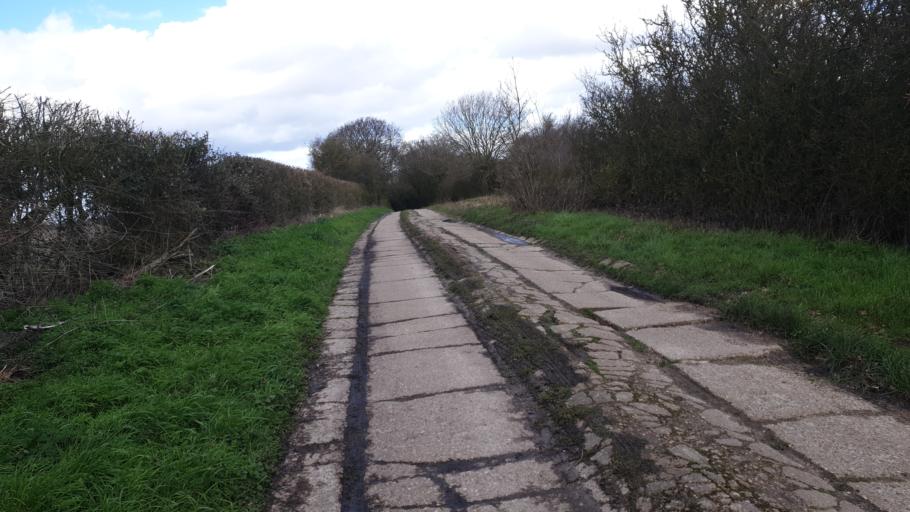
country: GB
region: England
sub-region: Essex
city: Little Clacton
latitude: 51.8306
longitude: 1.1717
